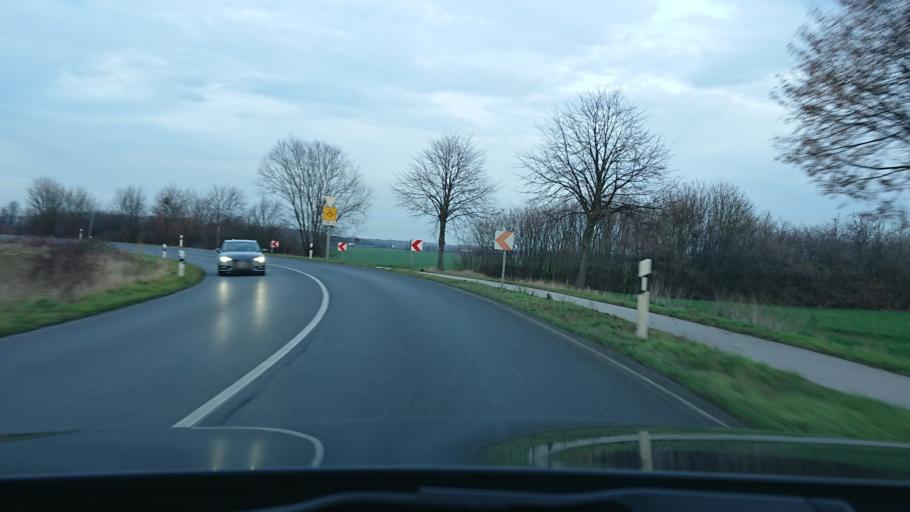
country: DE
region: North Rhine-Westphalia
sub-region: Regierungsbezirk Koln
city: Sinnersdorf
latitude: 51.0296
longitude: 6.8257
